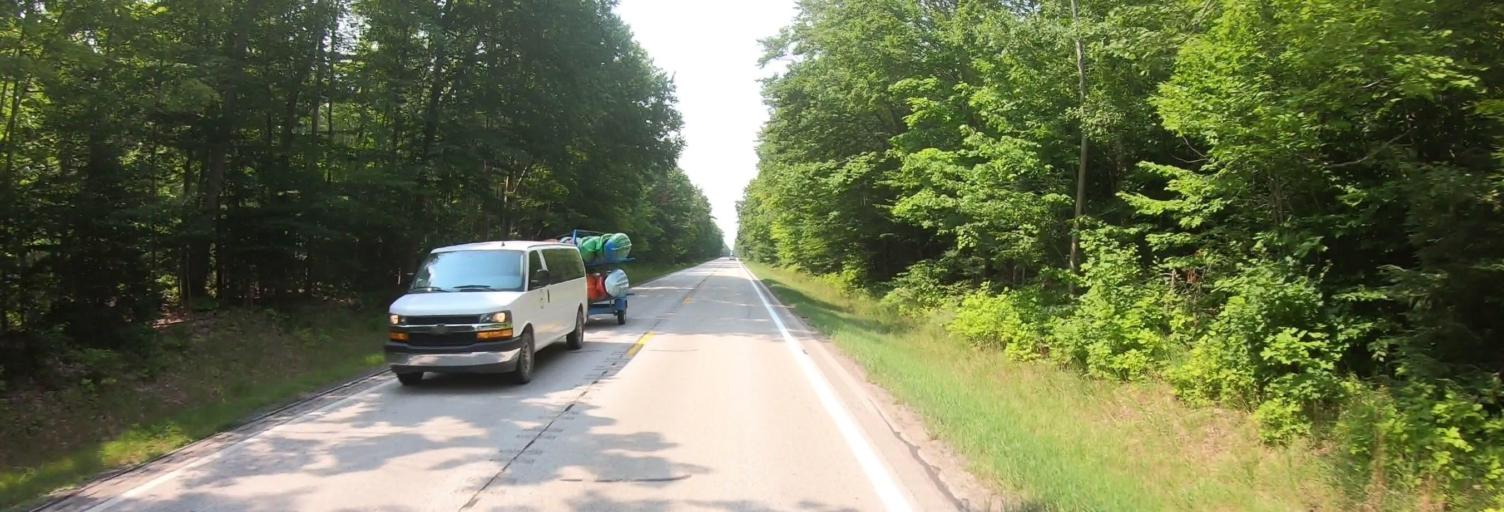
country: US
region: Michigan
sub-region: Luce County
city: Newberry
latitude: 46.5329
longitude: -85.3977
